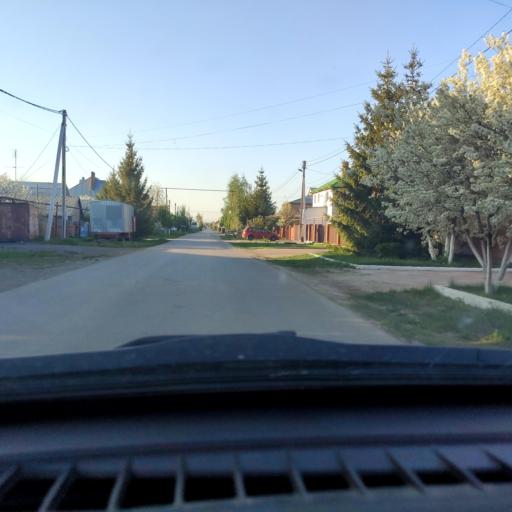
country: RU
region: Samara
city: Tol'yatti
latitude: 53.5609
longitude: 49.4024
